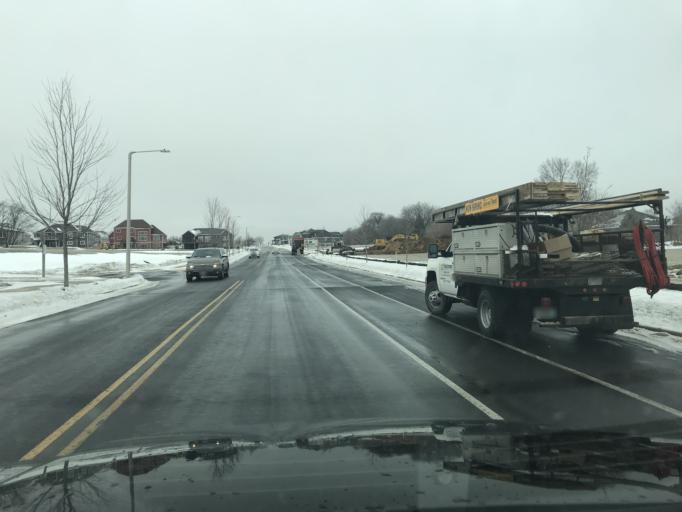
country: US
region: Wisconsin
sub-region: Dane County
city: Cottage Grove
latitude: 43.0917
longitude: -89.2203
